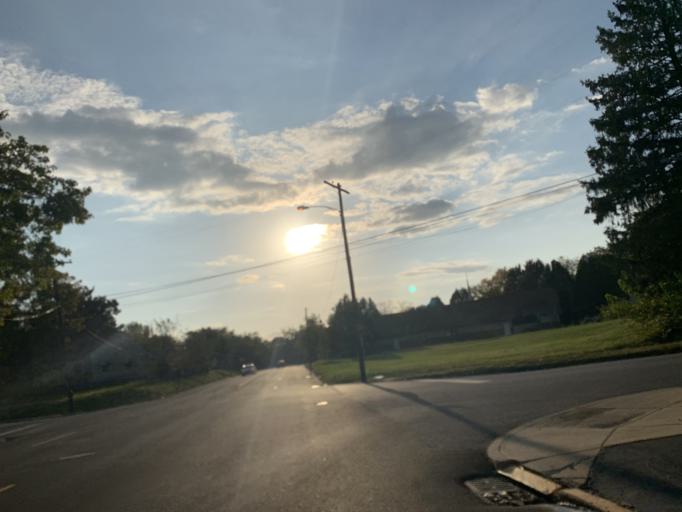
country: US
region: Kentucky
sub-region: Jefferson County
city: Shively
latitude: 38.2324
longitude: -85.8007
